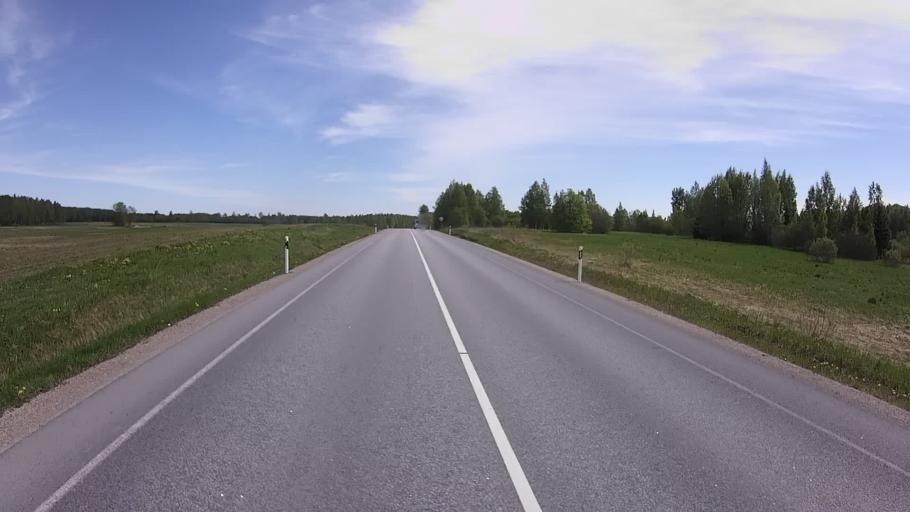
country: EE
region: Valgamaa
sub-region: Valga linn
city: Valga
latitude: 57.7233
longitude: 26.1900
